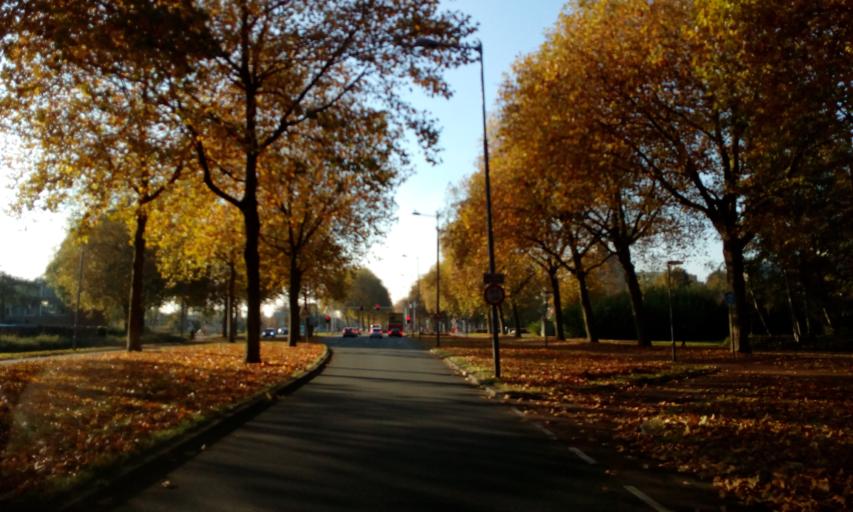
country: NL
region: South Holland
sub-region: Gemeente Rotterdam
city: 's-Gravenland
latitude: 51.9597
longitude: 4.5508
